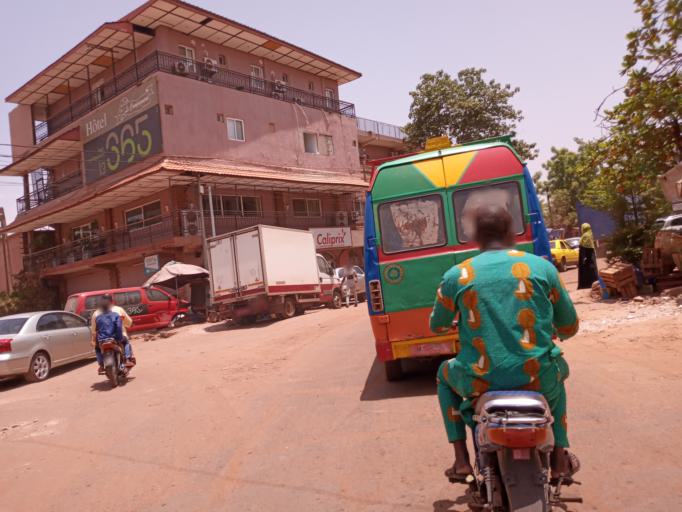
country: ML
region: Bamako
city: Bamako
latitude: 12.6472
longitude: -7.9786
